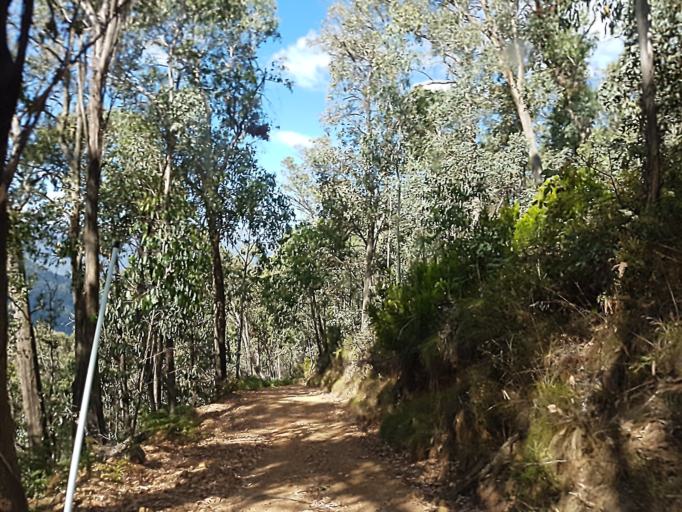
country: AU
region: Victoria
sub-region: Alpine
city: Mount Beauty
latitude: -36.9338
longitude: 147.0002
